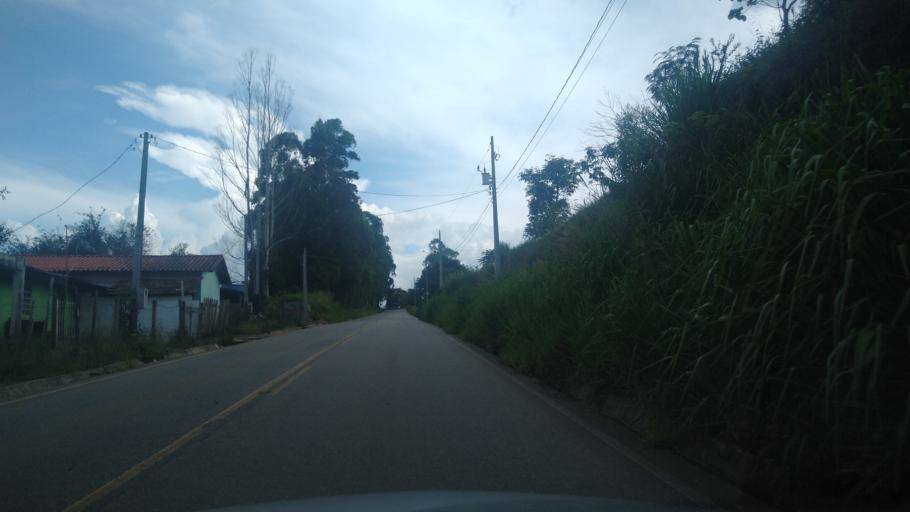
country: BR
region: Minas Gerais
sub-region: Extrema
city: Extrema
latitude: -22.7941
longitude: -46.3169
